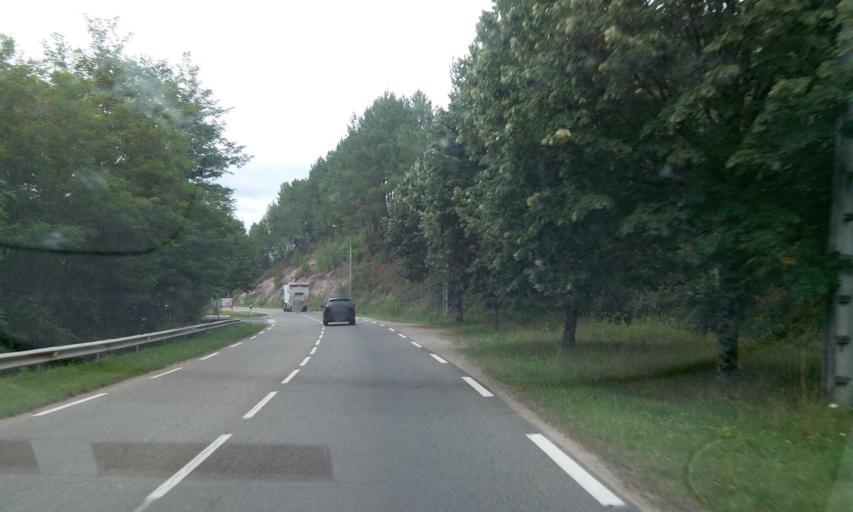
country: FR
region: Limousin
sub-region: Departement de la Correze
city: Brive-la-Gaillarde
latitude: 45.1389
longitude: 1.5493
